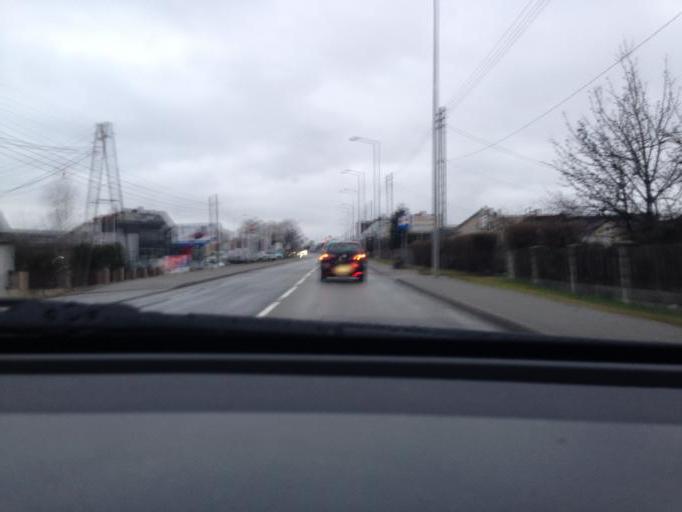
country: PL
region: Opole Voivodeship
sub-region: Powiat opolski
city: Opole
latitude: 50.6920
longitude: 17.9522
